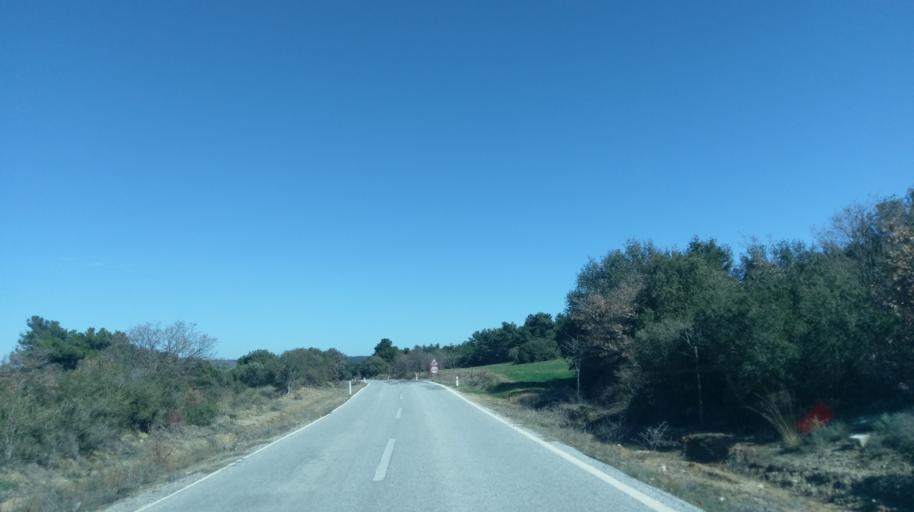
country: TR
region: Canakkale
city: Intepe
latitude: 40.1119
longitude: 26.2508
